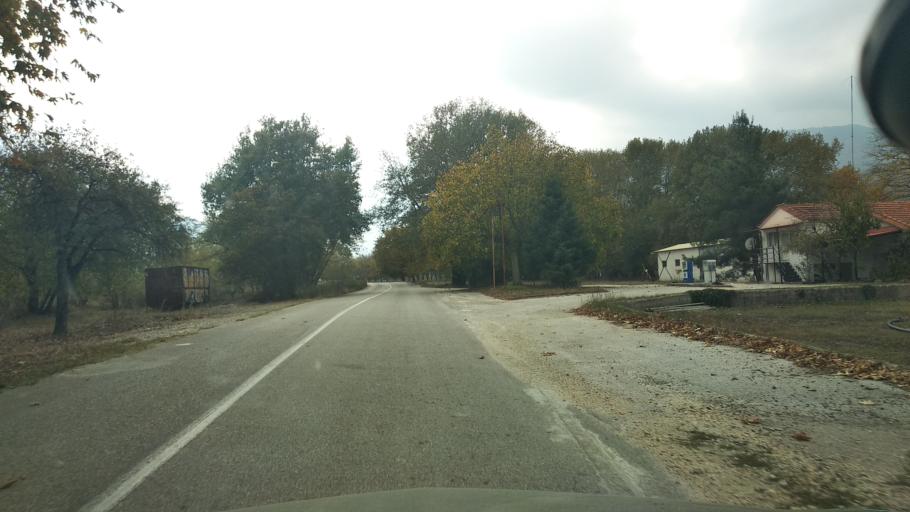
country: GR
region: Thessaly
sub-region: Trikala
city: Kastraki
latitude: 39.7162
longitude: 21.5262
